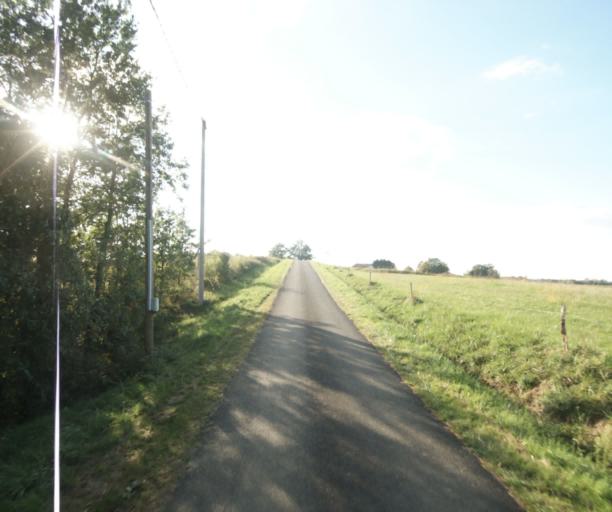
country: FR
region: Midi-Pyrenees
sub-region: Departement du Gers
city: Eauze
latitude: 43.7506
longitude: 0.1064
